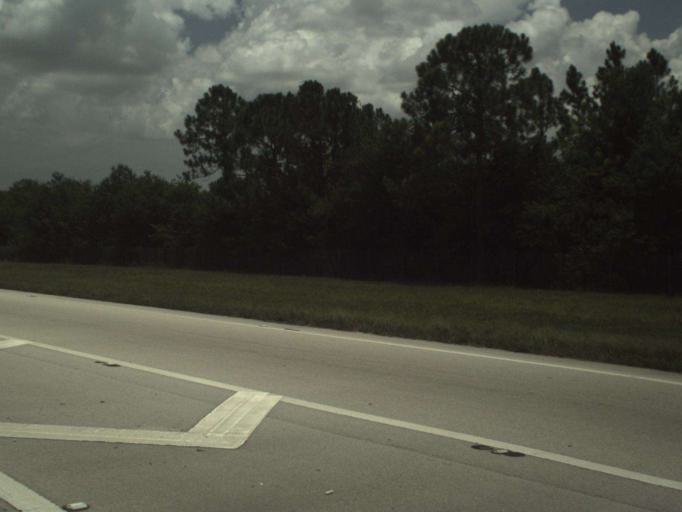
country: US
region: Florida
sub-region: Saint Lucie County
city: Fort Pierce South
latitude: 27.3744
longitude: -80.4062
